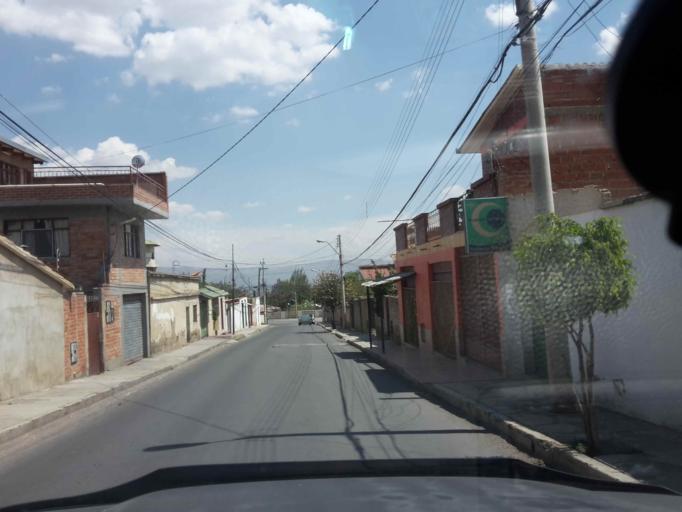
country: BO
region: Cochabamba
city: Cochabamba
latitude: -17.3473
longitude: -66.1949
